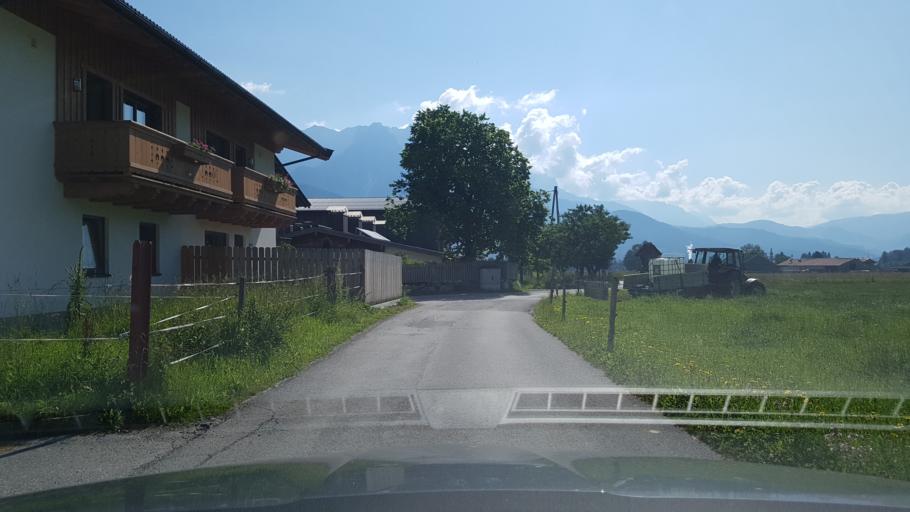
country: AT
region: Salzburg
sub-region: Politischer Bezirk Zell am See
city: Leogang
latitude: 47.4443
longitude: 12.7898
